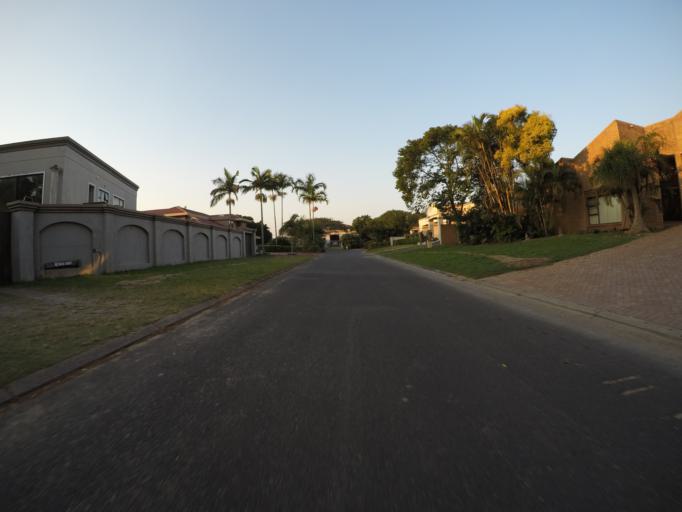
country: ZA
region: KwaZulu-Natal
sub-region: uThungulu District Municipality
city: Richards Bay
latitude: -28.7662
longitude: 32.1131
